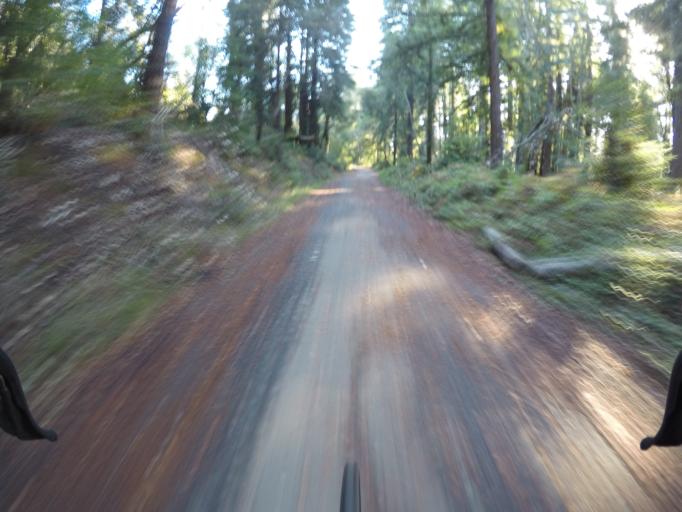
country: US
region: California
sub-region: Santa Cruz County
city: Pasatiempo
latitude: 37.0193
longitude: -122.0444
